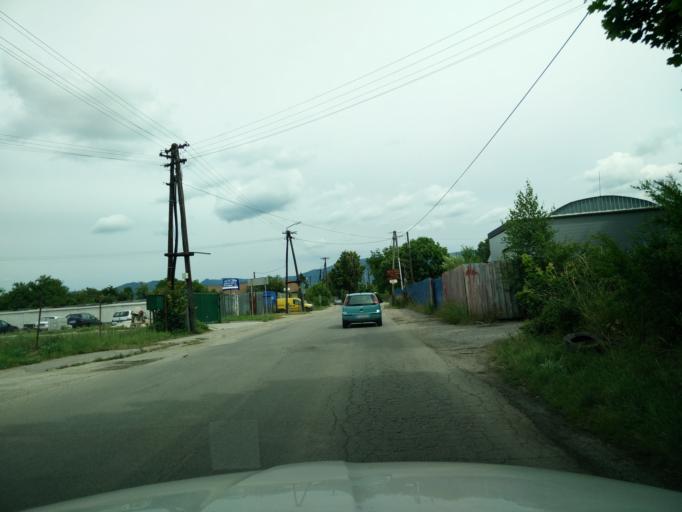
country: SK
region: Nitriansky
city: Bojnice
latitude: 48.7476
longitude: 18.5738
